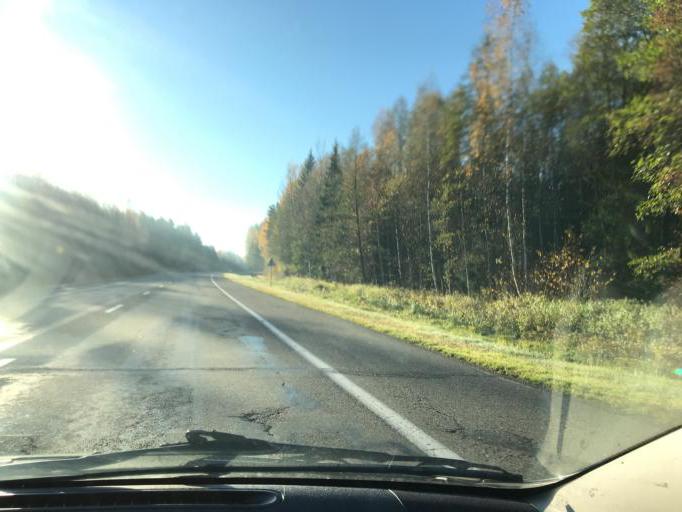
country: BY
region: Vitebsk
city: Vitebsk
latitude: 54.8921
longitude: 30.3836
